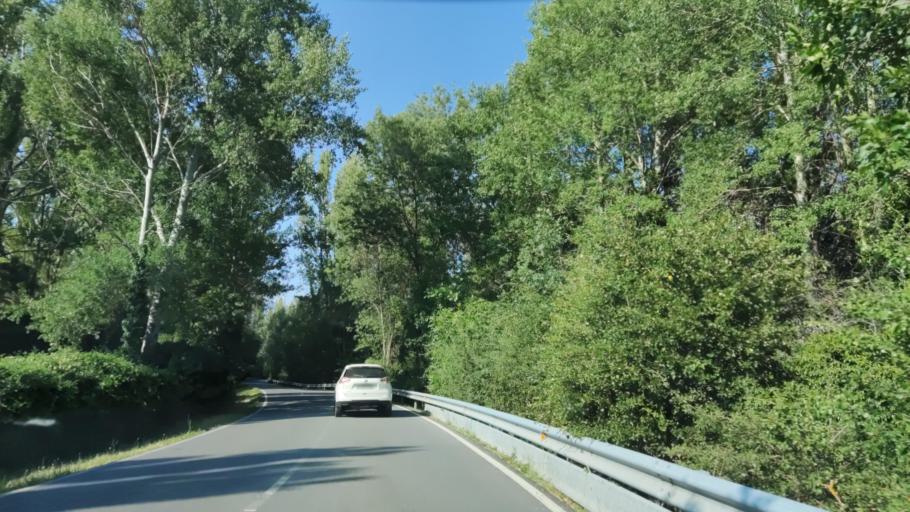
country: ES
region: Madrid
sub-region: Provincia de Madrid
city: Rascafria
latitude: 40.8892
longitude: -3.8855
